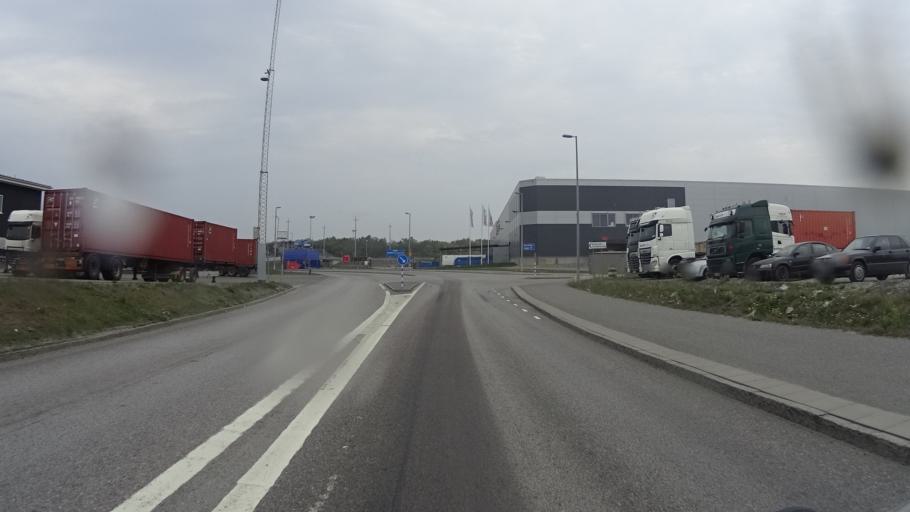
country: SE
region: Vaestra Goetaland
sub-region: Goteborg
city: Majorna
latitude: 57.7007
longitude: 11.8617
